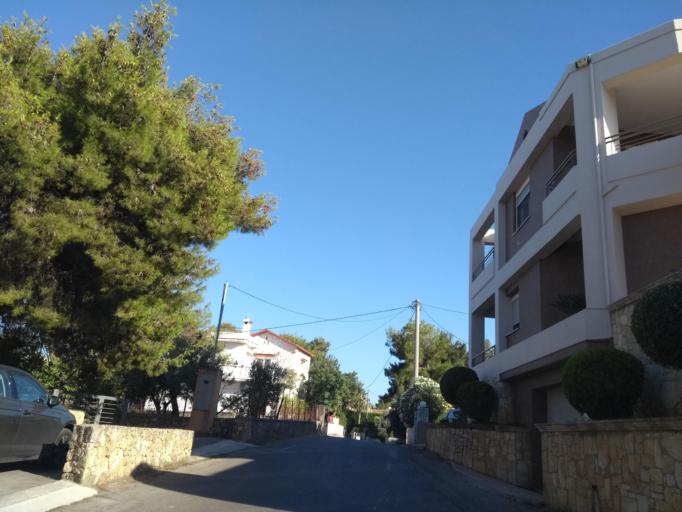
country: GR
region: Crete
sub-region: Nomos Chanias
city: Pithari
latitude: 35.5214
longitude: 24.0778
